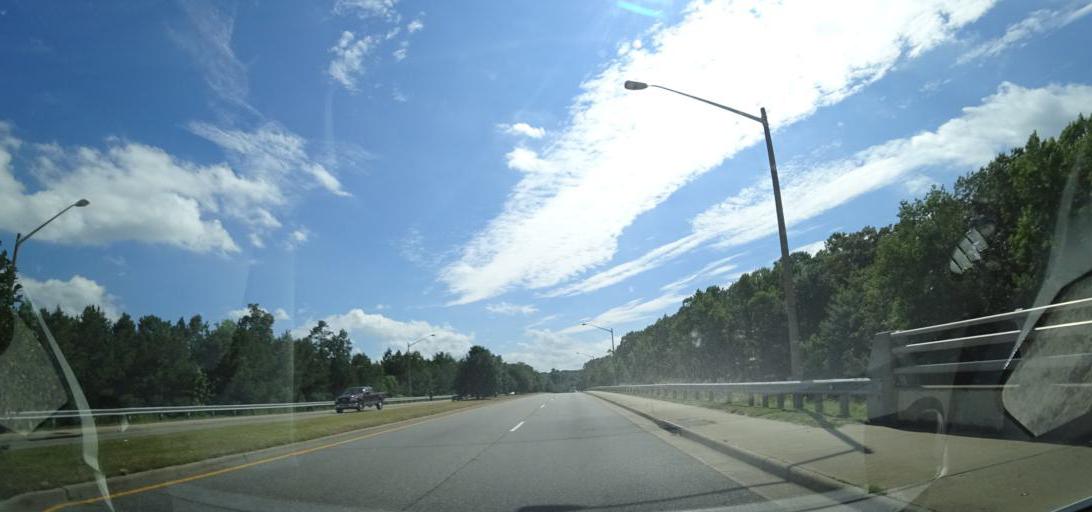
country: US
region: Virginia
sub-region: York County
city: Yorktown
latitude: 37.1245
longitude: -76.5187
